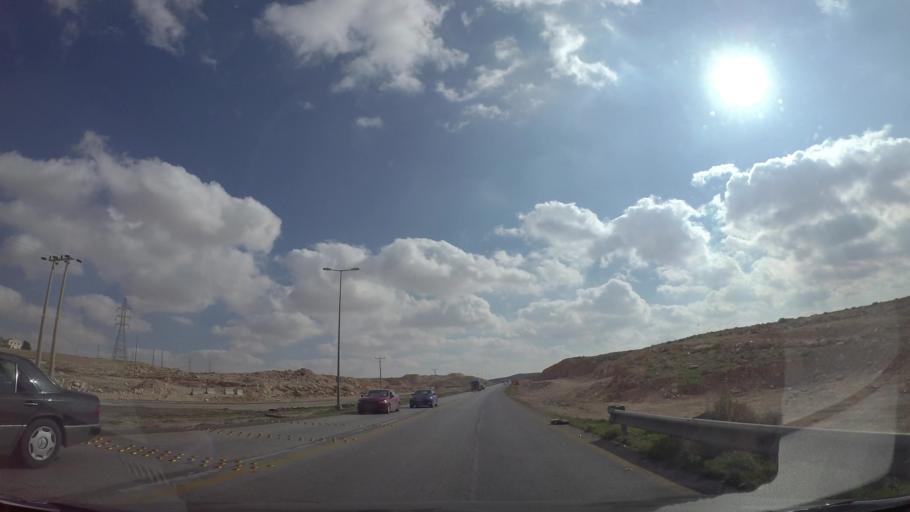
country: JO
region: Amman
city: Al Jizah
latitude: 31.6025
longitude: 35.9985
